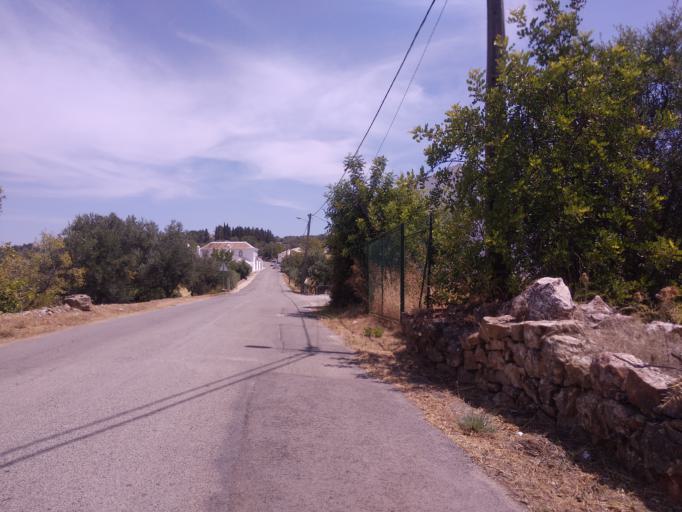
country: PT
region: Faro
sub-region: Sao Bras de Alportel
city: Sao Bras de Alportel
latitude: 37.1476
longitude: -7.9326
